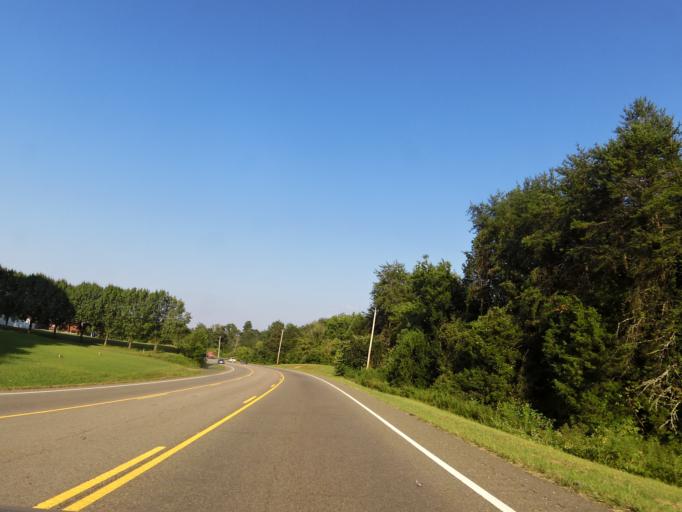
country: US
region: Tennessee
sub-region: Knox County
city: Knoxville
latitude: 35.9013
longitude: -83.8516
